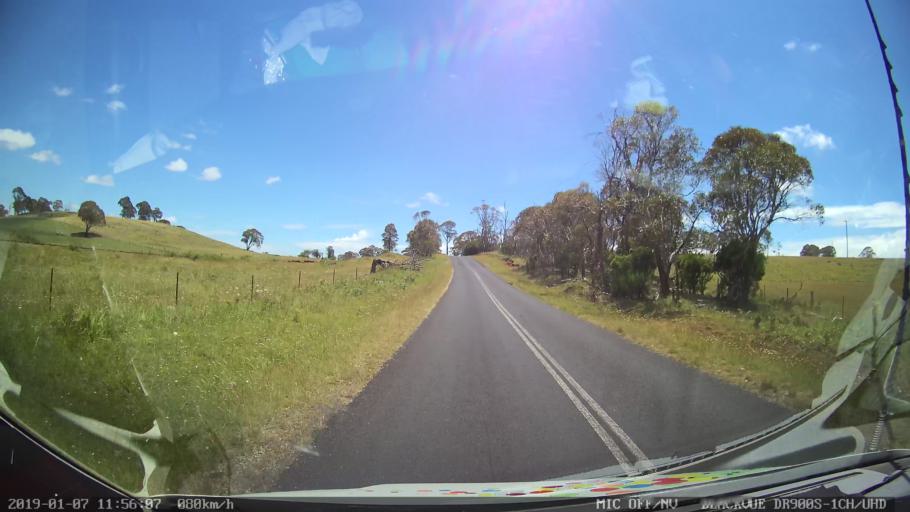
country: AU
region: New South Wales
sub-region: Guyra
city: Guyra
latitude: -30.2782
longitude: 151.6738
